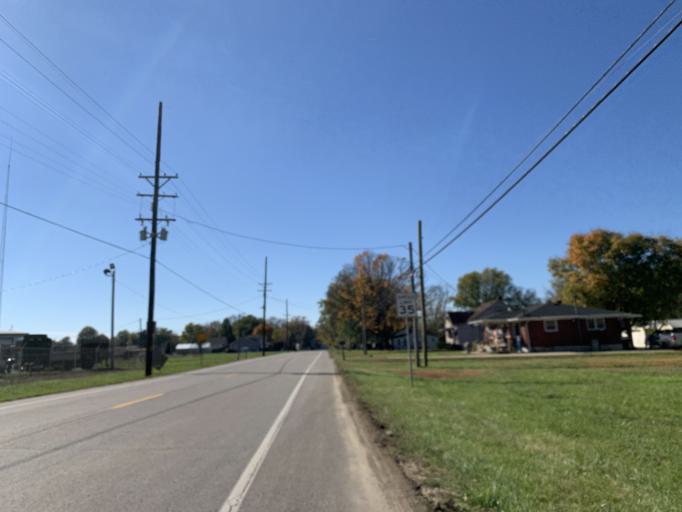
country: US
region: Kentucky
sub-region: Jefferson County
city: Shively
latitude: 38.2142
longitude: -85.8263
